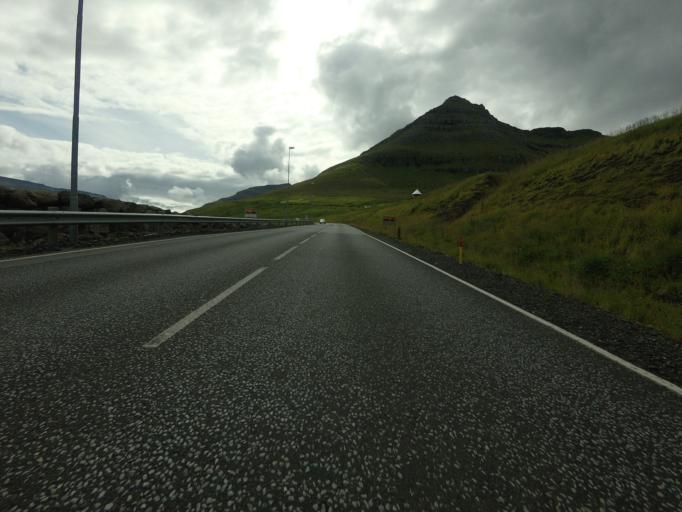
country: FO
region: Eysturoy
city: Eystur
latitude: 62.2104
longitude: -6.6987
